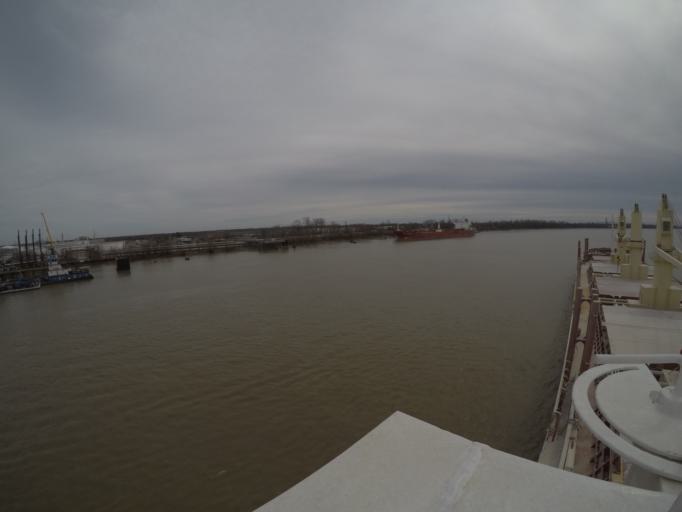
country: US
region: Louisiana
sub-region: Saint Charles Parish
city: Hahnville
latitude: 29.9856
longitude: -90.4008
